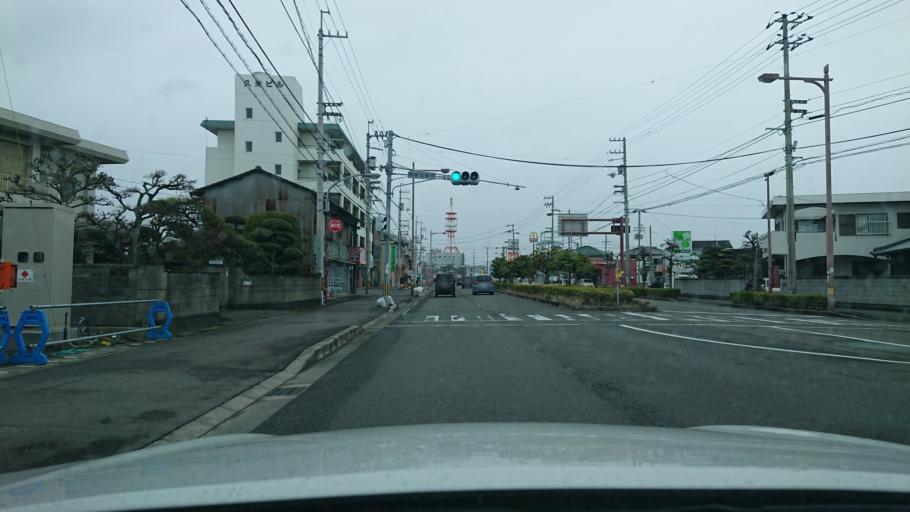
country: JP
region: Tokushima
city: Tokushima-shi
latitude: 34.0846
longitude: 134.5214
